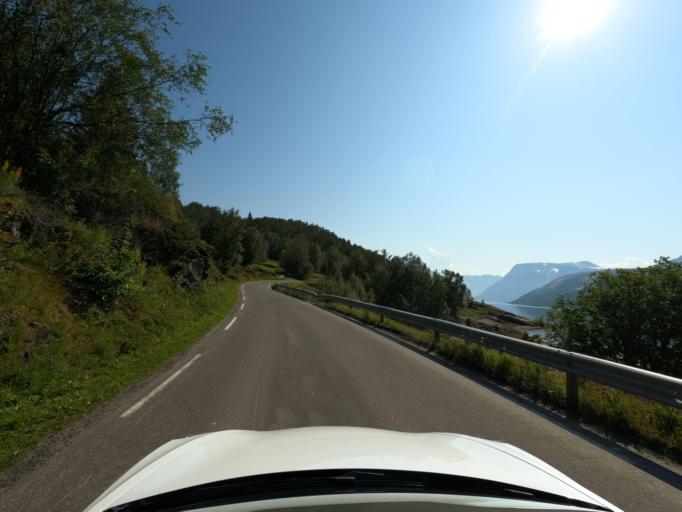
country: NO
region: Nordland
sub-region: Narvik
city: Narvik
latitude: 68.2946
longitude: 17.3561
